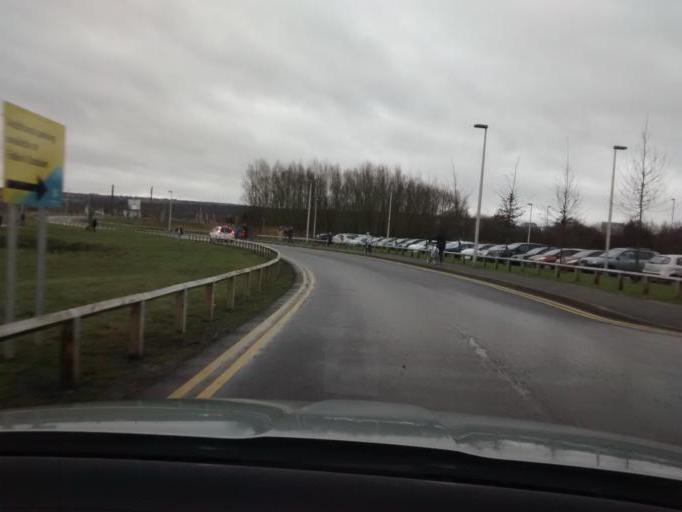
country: GB
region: Scotland
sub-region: Falkirk
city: Falkirk
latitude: 56.0139
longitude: -3.7593
